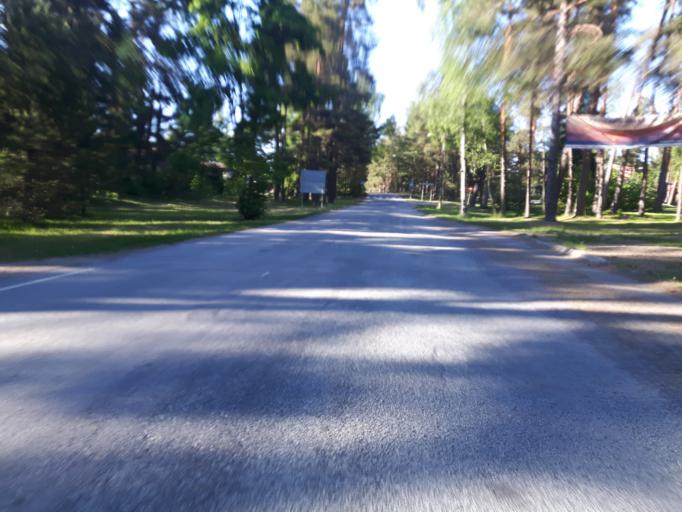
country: EE
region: Harju
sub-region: Loksa linn
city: Loksa
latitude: 59.5765
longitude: 25.9705
